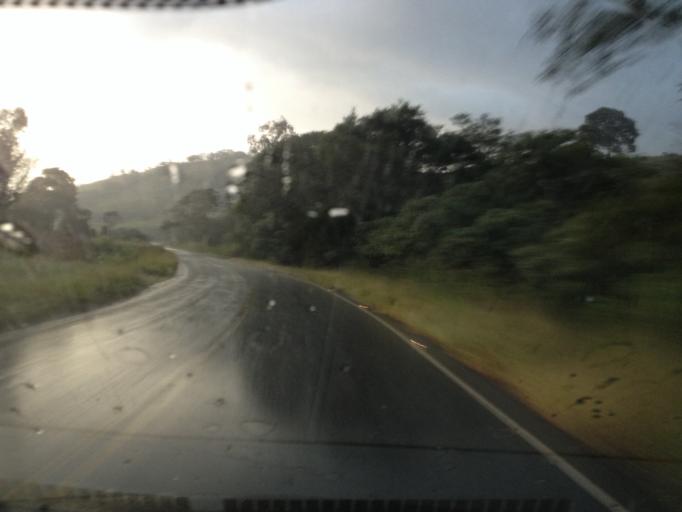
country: BR
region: Minas Gerais
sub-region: Caxambu
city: Caxambu
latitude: -21.9812
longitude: -44.9843
